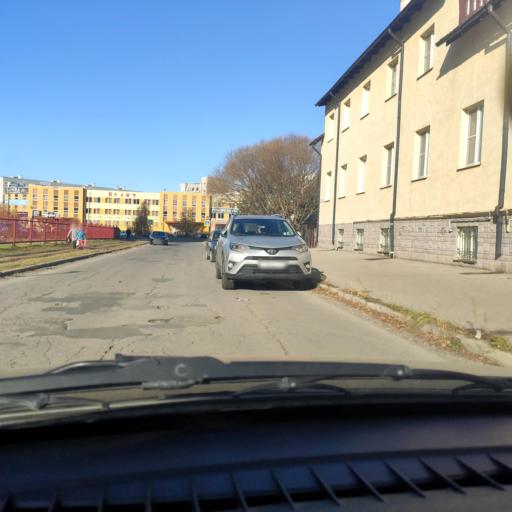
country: RU
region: Samara
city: Tol'yatti
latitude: 53.5395
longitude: 49.3633
